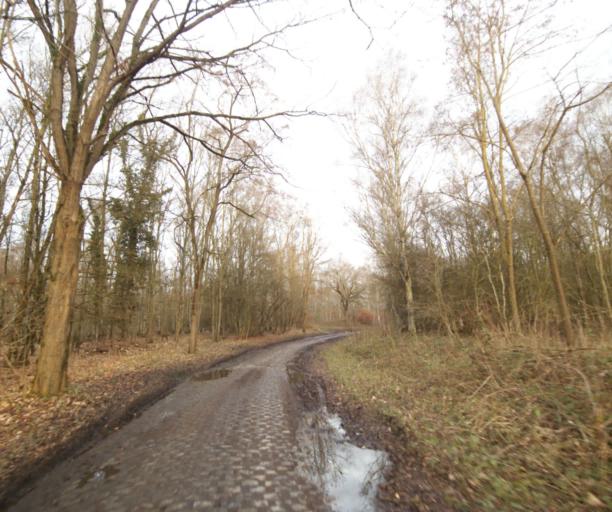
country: BE
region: Wallonia
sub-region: Province du Hainaut
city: Bernissart
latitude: 50.4599
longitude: 3.6240
